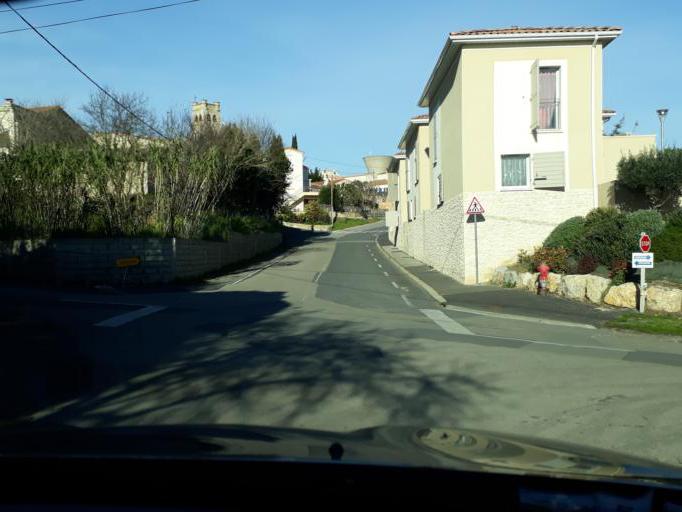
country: FR
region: Languedoc-Roussillon
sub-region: Departement de l'Herault
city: Castelnau-de-Guers
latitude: 43.4335
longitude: 3.4400
